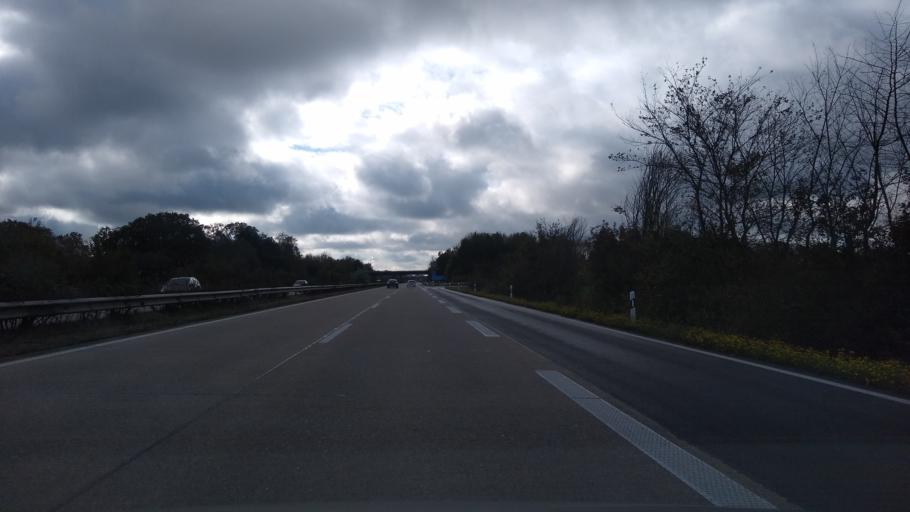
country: DE
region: Lower Saxony
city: Grossenkneten
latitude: 52.9544
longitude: 8.1811
